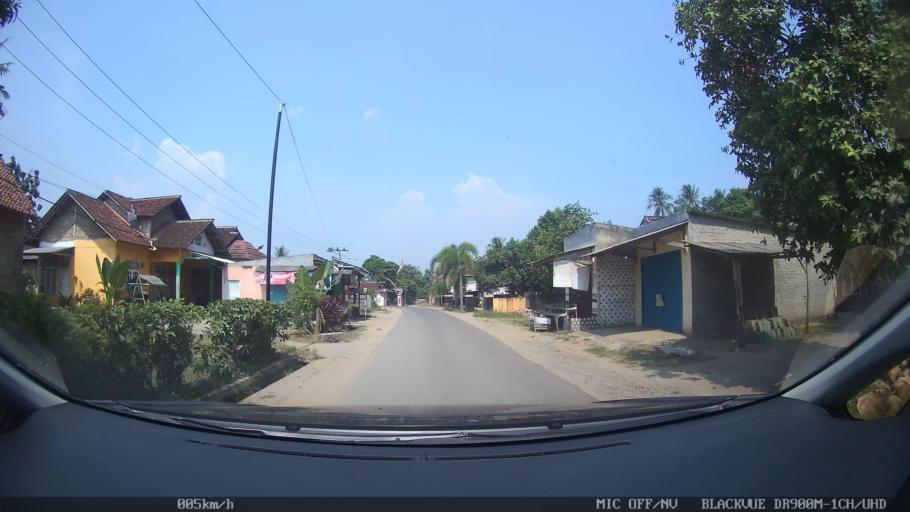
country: ID
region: Lampung
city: Natar
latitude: -5.3091
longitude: 105.2130
